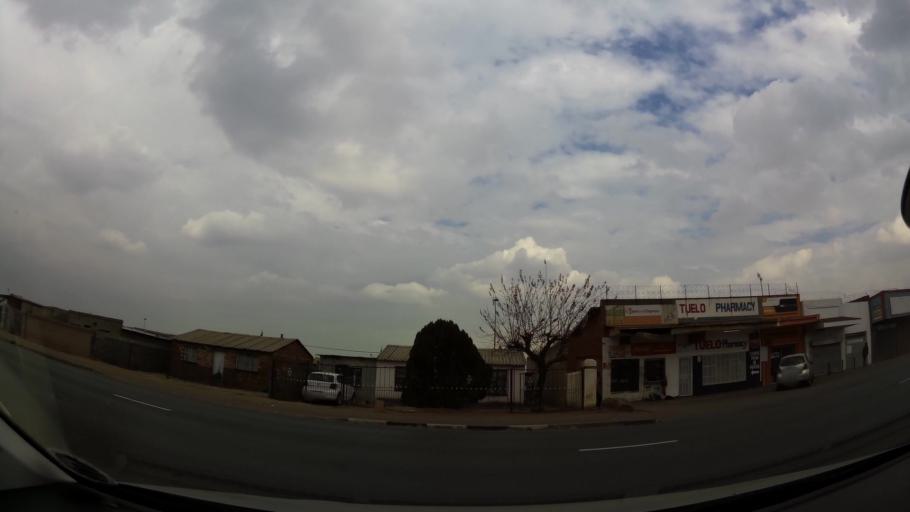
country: ZA
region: Gauteng
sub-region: City of Johannesburg Metropolitan Municipality
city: Soweto
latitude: -26.2594
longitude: 27.8584
